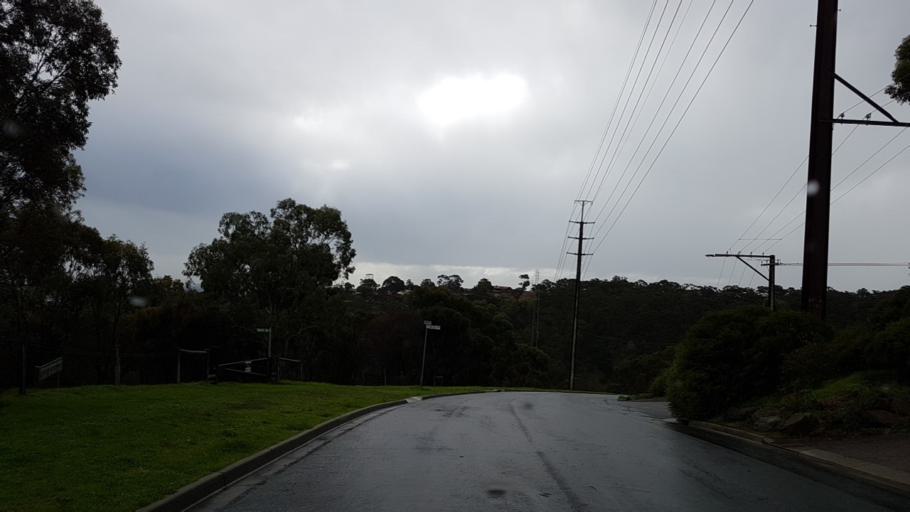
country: AU
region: South Australia
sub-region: Onkaparinga
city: Bedford Park
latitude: -35.0407
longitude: 138.5782
